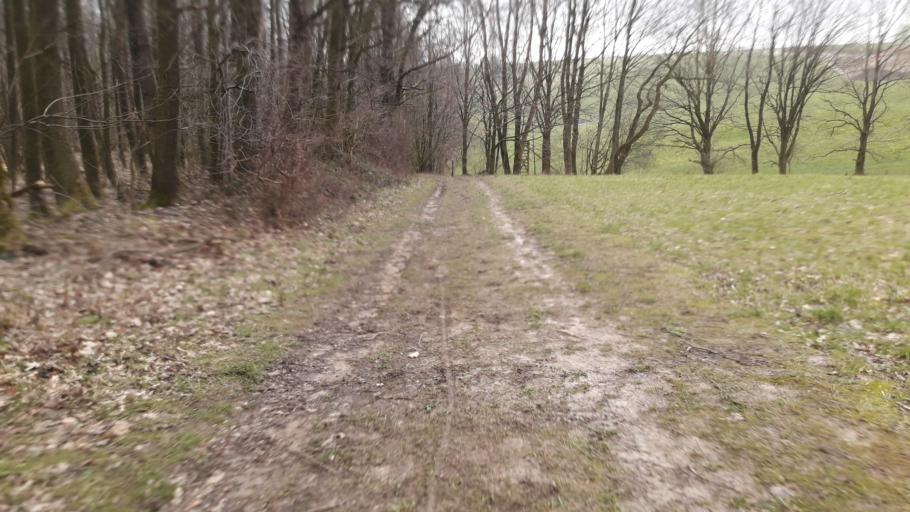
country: DE
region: North Rhine-Westphalia
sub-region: Regierungsbezirk Detmold
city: Altenbeken
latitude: 51.7341
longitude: 8.8941
